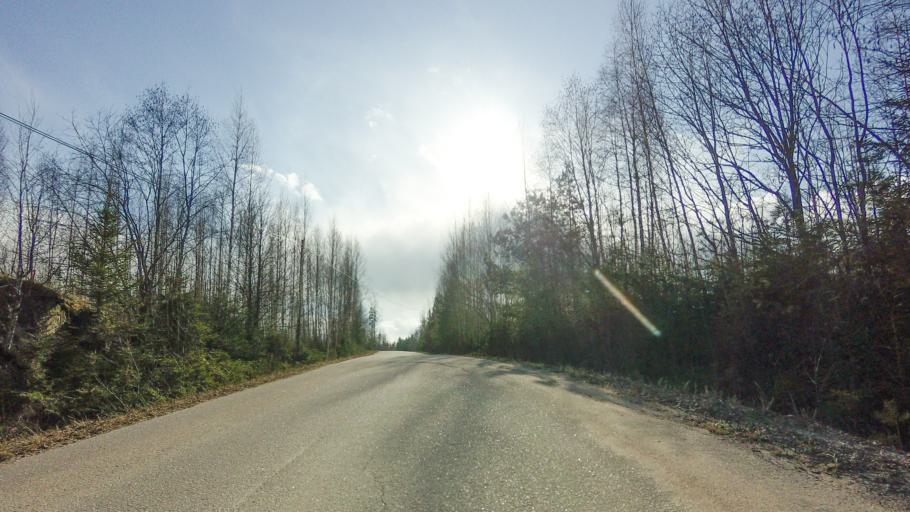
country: FI
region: Varsinais-Suomi
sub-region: Salo
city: Suomusjaervi
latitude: 60.3018
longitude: 23.6449
